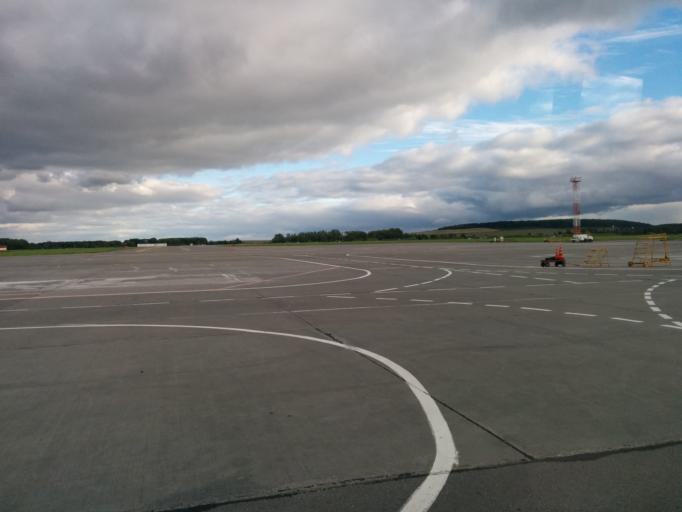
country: RU
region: Perm
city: Kultayevo
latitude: 57.9193
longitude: 56.0204
